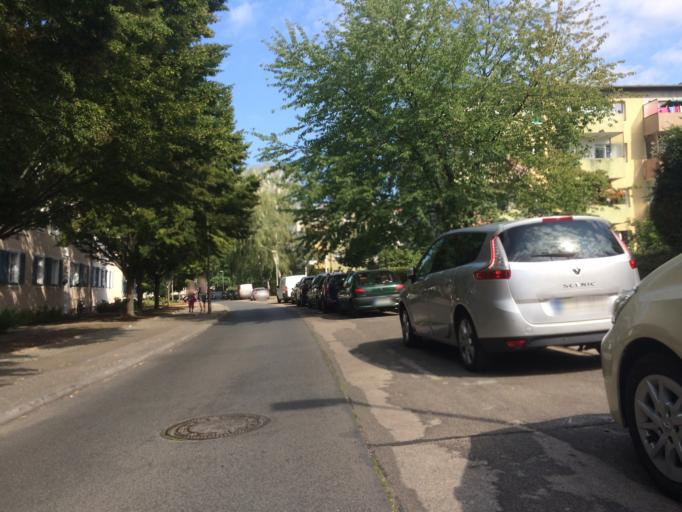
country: DE
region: Berlin
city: Wedding Bezirk
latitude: 52.5603
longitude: 13.3568
